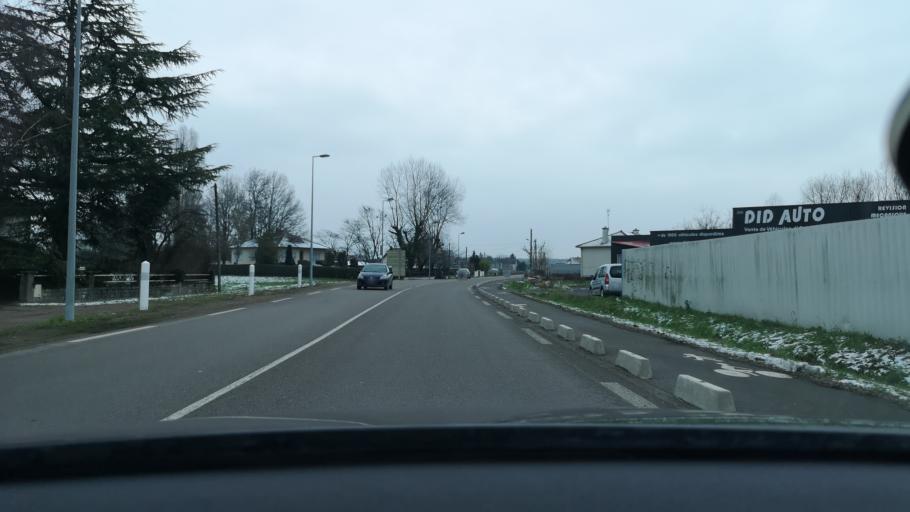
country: FR
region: Bourgogne
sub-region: Departement de Saone-et-Loire
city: Saint-Marcel
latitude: 46.7828
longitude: 4.9119
